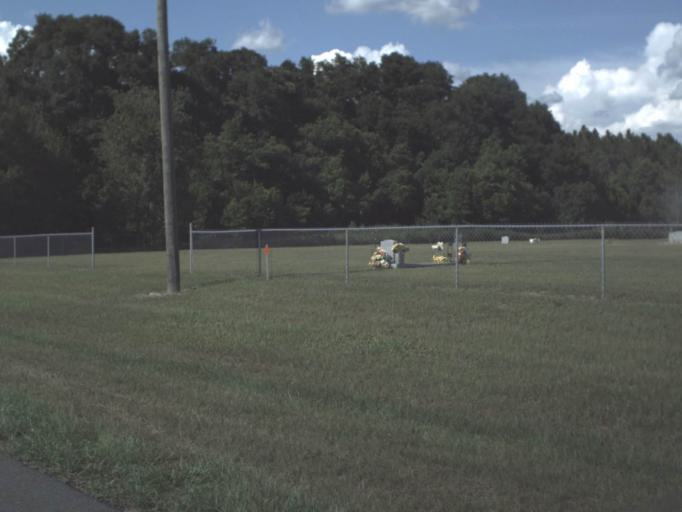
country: US
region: Florida
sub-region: Lafayette County
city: Mayo
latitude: 30.0790
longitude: -83.1735
